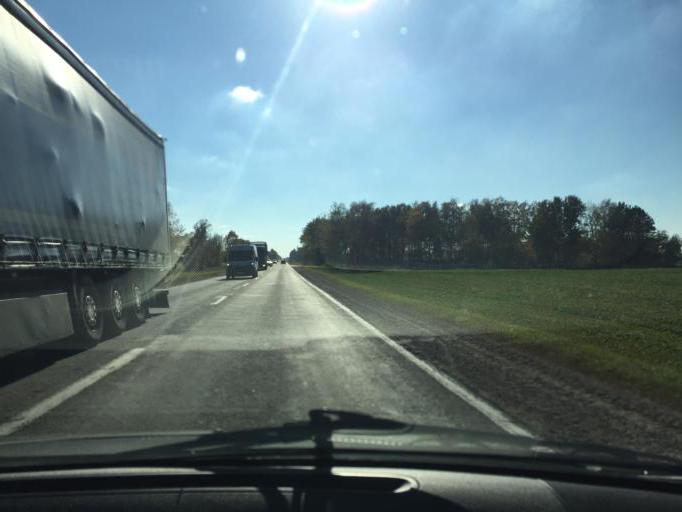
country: BY
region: Minsk
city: Salihorsk
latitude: 52.9104
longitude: 27.4794
